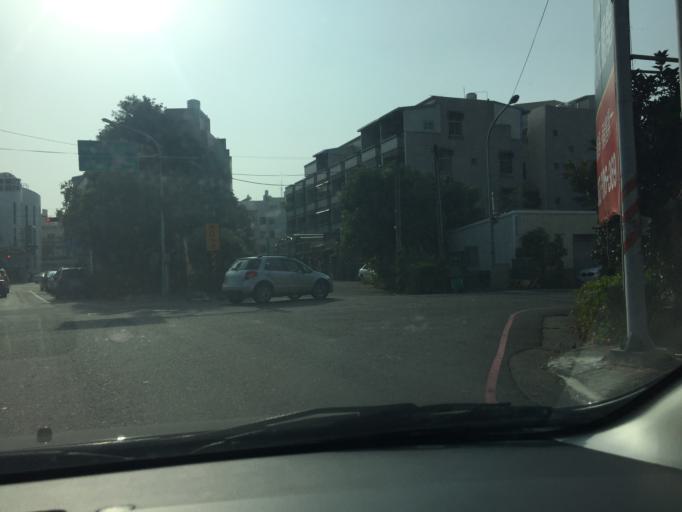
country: TW
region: Taiwan
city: Xinying
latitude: 23.1842
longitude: 120.2559
